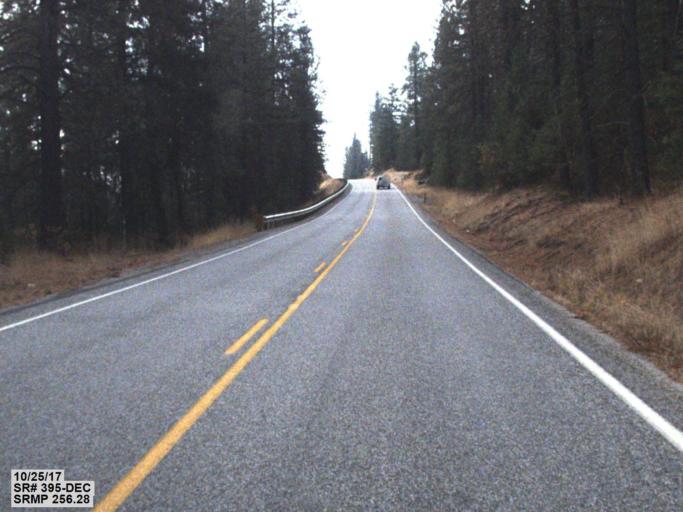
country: US
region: Washington
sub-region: Stevens County
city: Kettle Falls
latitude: 48.8193
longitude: -118.1695
